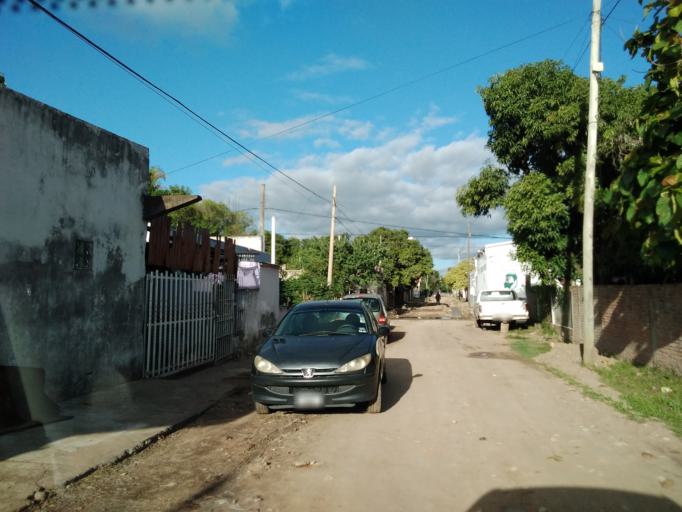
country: AR
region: Corrientes
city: Corrientes
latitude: -27.4780
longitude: -58.8114
